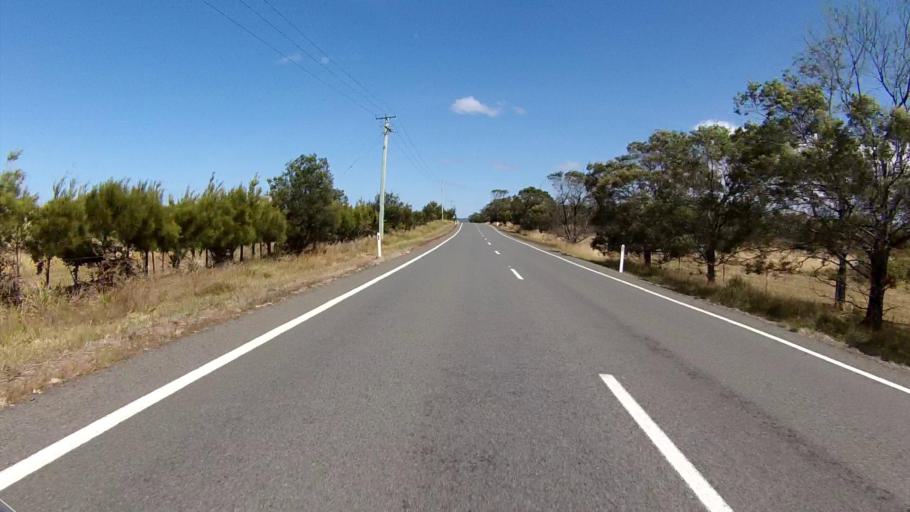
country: AU
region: Tasmania
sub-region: Break O'Day
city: St Helens
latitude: -42.0930
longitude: 148.0652
